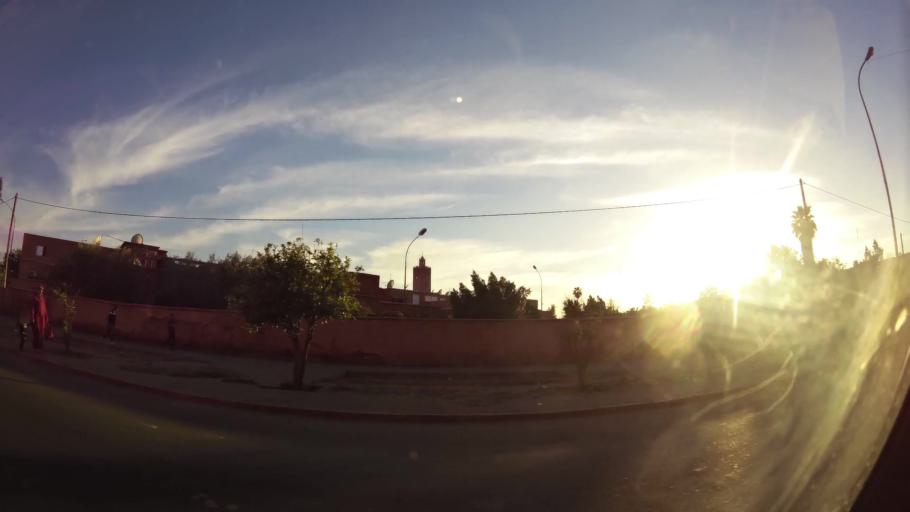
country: MA
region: Marrakech-Tensift-Al Haouz
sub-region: Marrakech
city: Marrakesh
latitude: 31.6199
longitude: -8.0266
